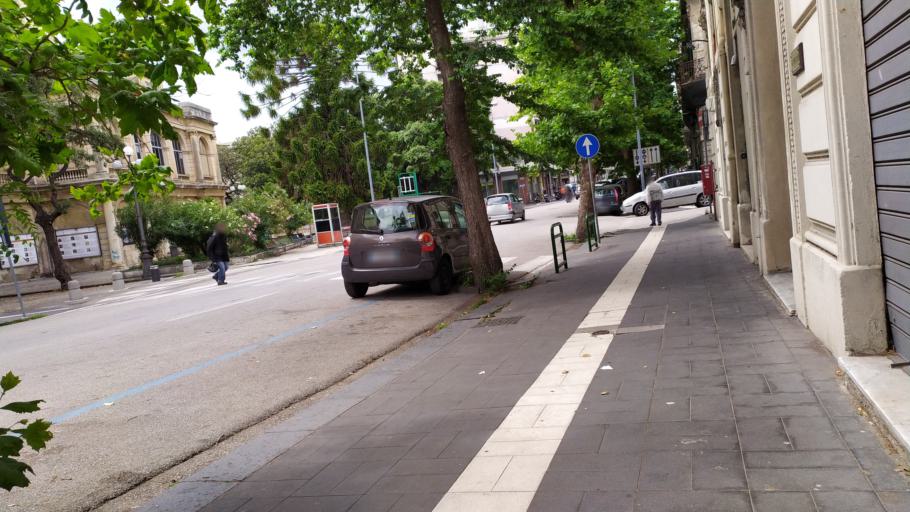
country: IT
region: Sicily
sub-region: Messina
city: Messina
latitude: 38.1962
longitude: 15.5557
